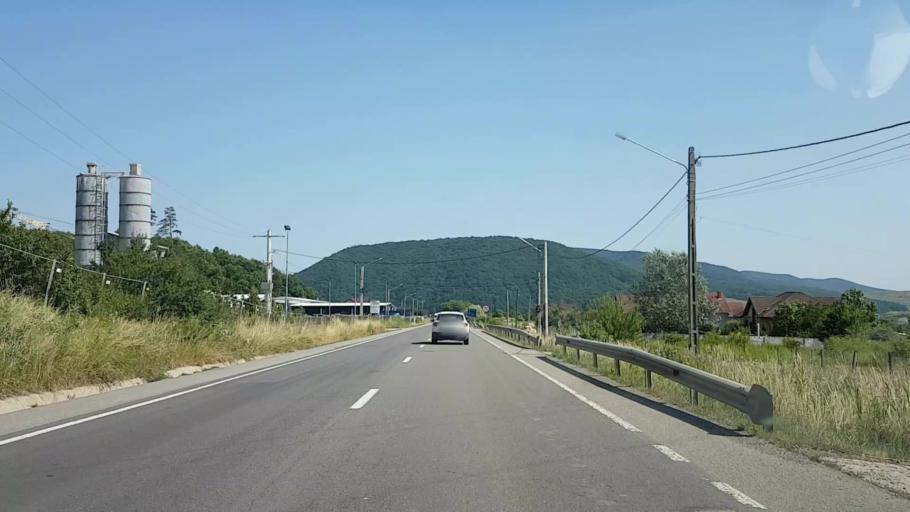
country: RO
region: Bistrita-Nasaud
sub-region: Comuna Sieu-Magherus
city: Sieu-Magherus
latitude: 47.0669
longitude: 24.4114
